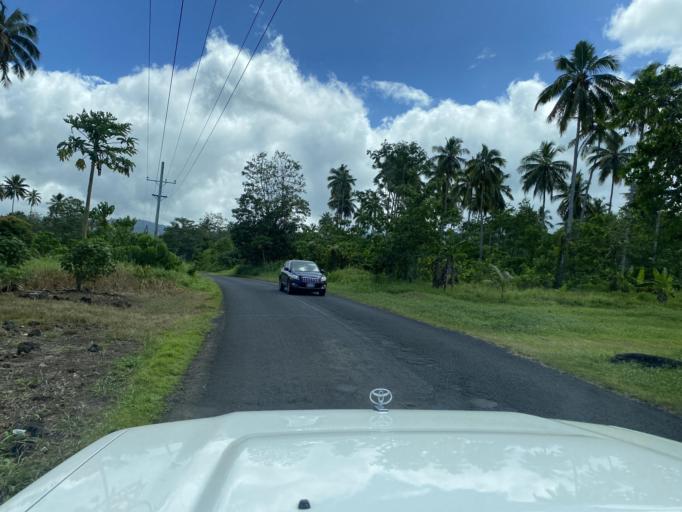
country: WS
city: Lotofaga
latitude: -14.0022
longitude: -171.7781
